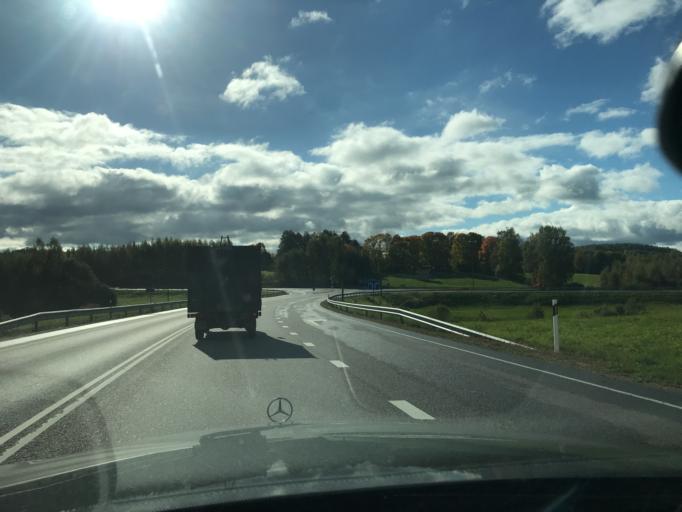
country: EE
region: Vorumaa
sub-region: Voru linn
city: Voru
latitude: 57.8115
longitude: 27.0649
